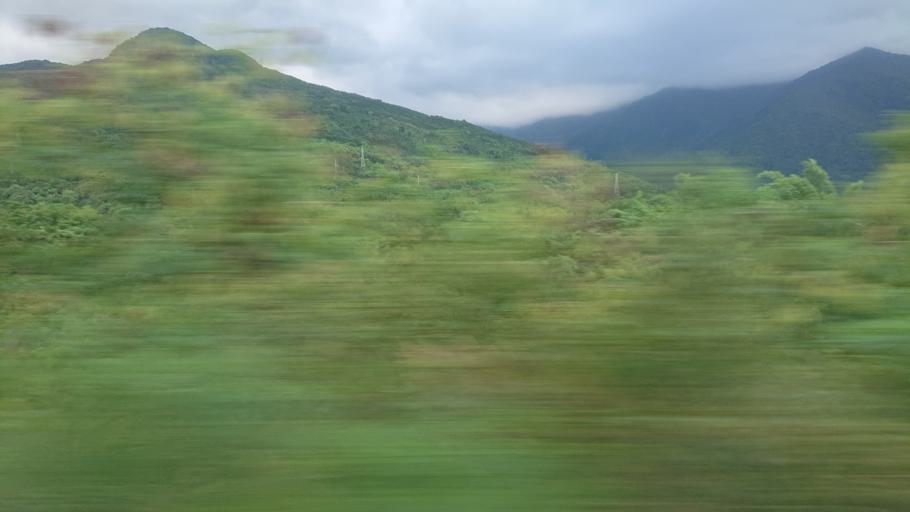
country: TW
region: Taiwan
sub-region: Hualien
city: Hualian
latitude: 23.6228
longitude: 121.3975
